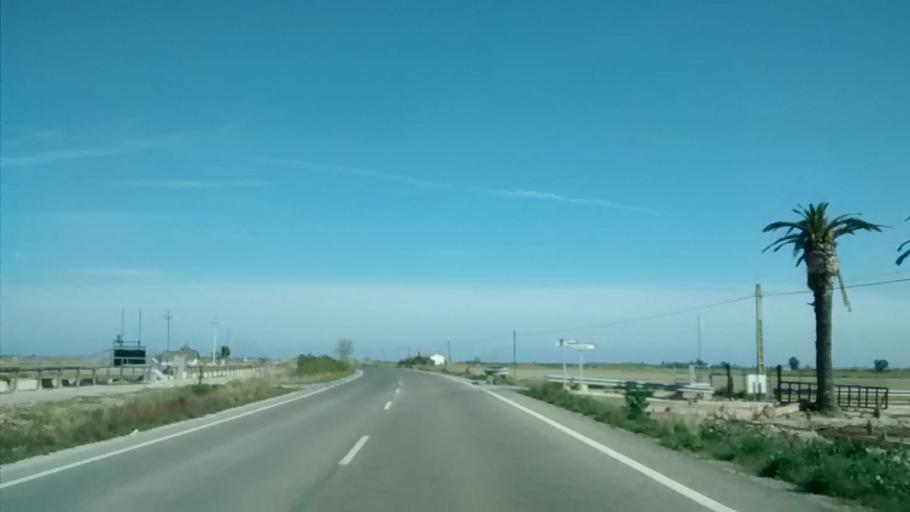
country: ES
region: Catalonia
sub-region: Provincia de Tarragona
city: Deltebre
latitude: 40.7069
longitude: 0.7654
